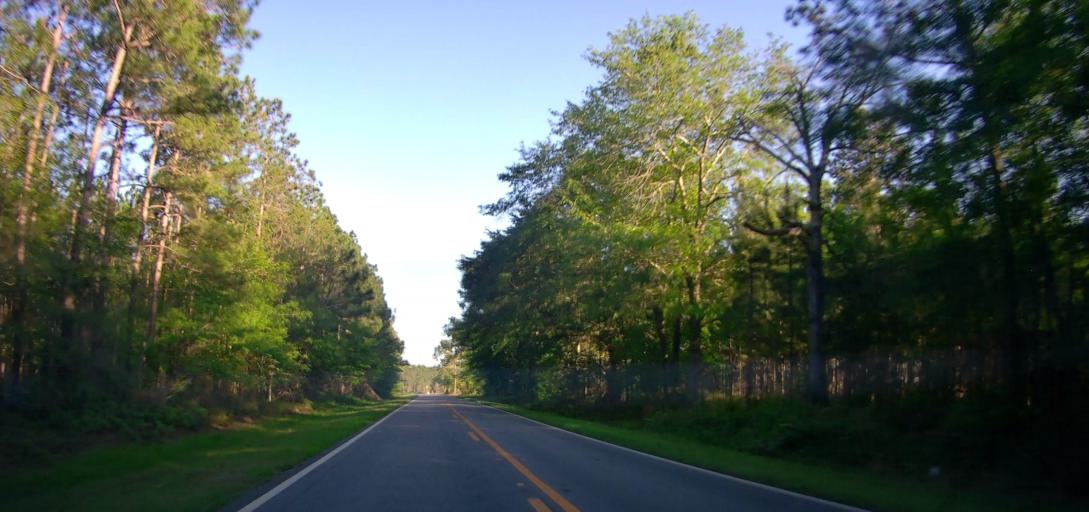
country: US
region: Georgia
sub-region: Ben Hill County
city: Fitzgerald
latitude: 31.6885
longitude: -83.2142
